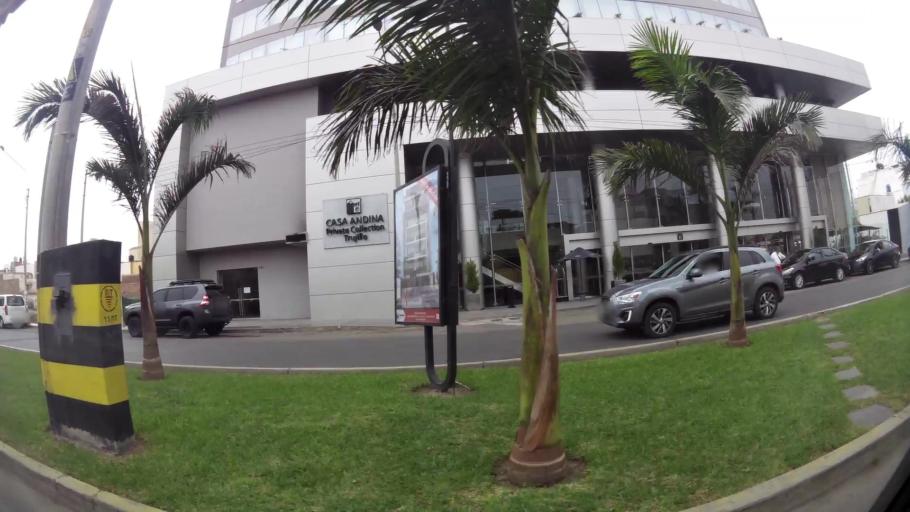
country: PE
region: La Libertad
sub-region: Provincia de Trujillo
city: Buenos Aires
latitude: -8.1372
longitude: -79.0345
